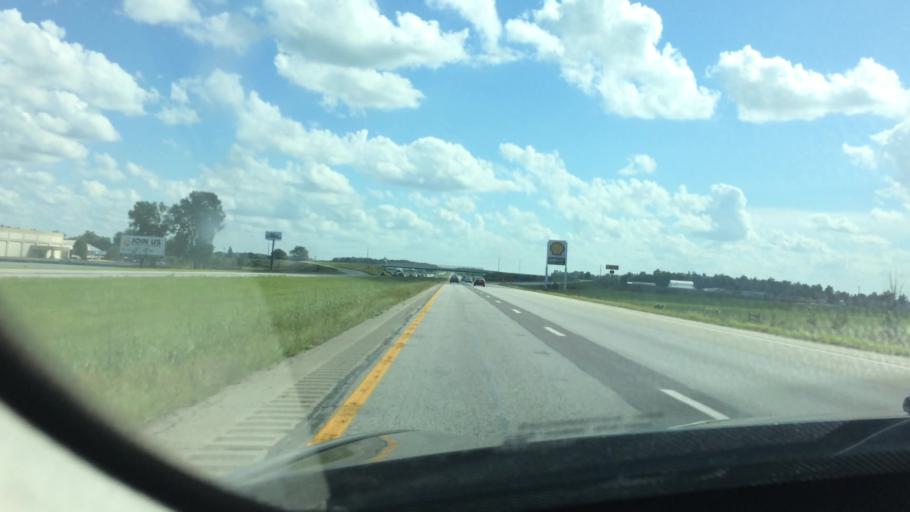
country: US
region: Ohio
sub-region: Shelby County
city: Botkins
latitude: 40.4728
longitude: -84.1694
